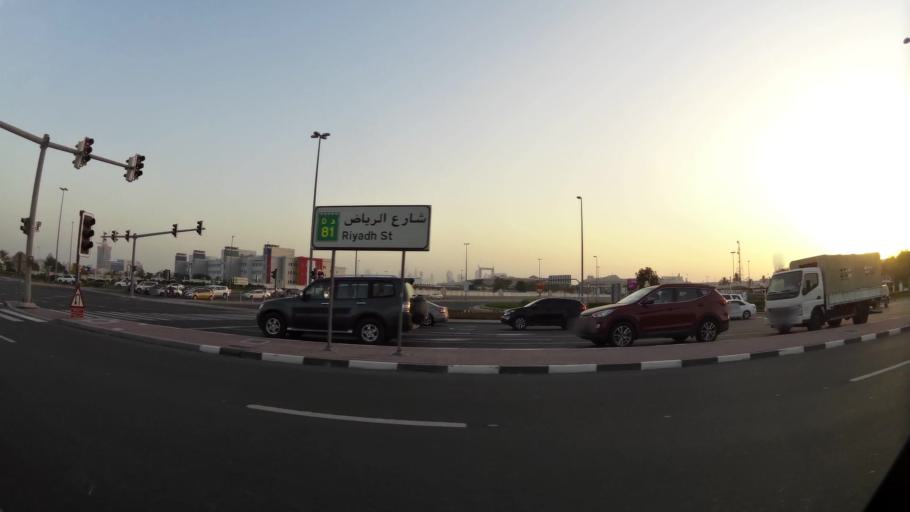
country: AE
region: Ash Shariqah
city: Sharjah
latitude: 25.2463
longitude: 55.3217
